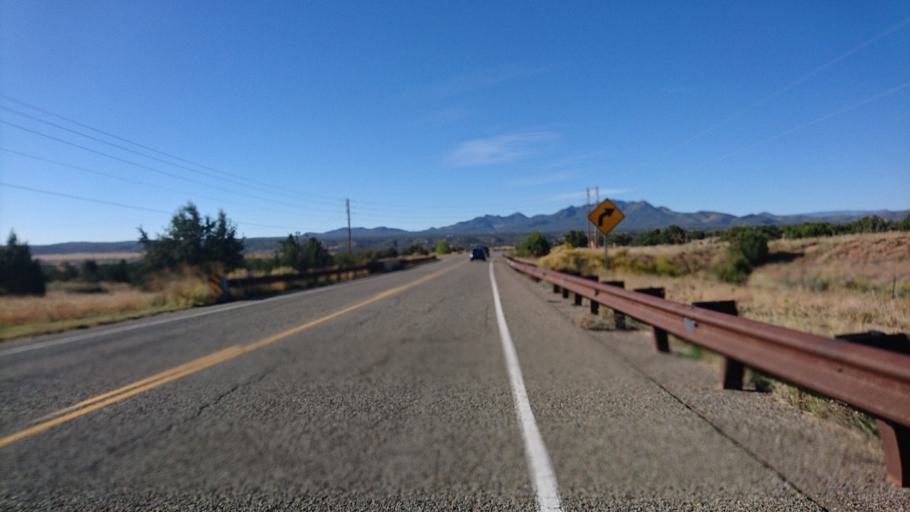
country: US
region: New Mexico
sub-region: Santa Fe County
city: La Cienega
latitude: 35.4361
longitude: -106.0828
